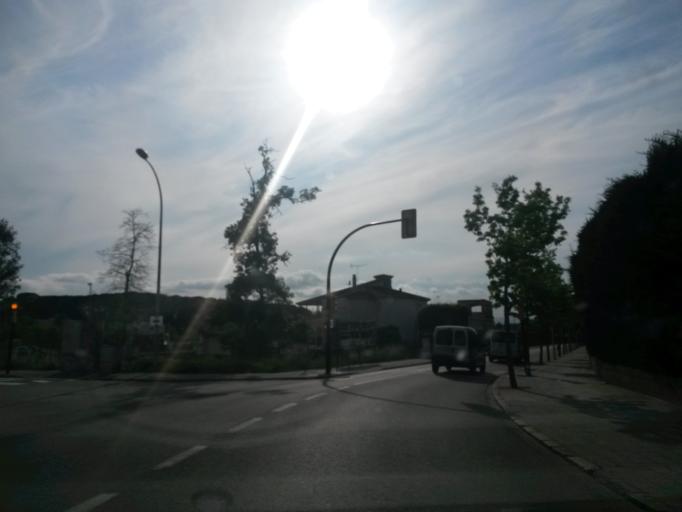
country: ES
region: Catalonia
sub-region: Provincia de Girona
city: Caldes de Malavella
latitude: 41.8375
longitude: 2.8064
